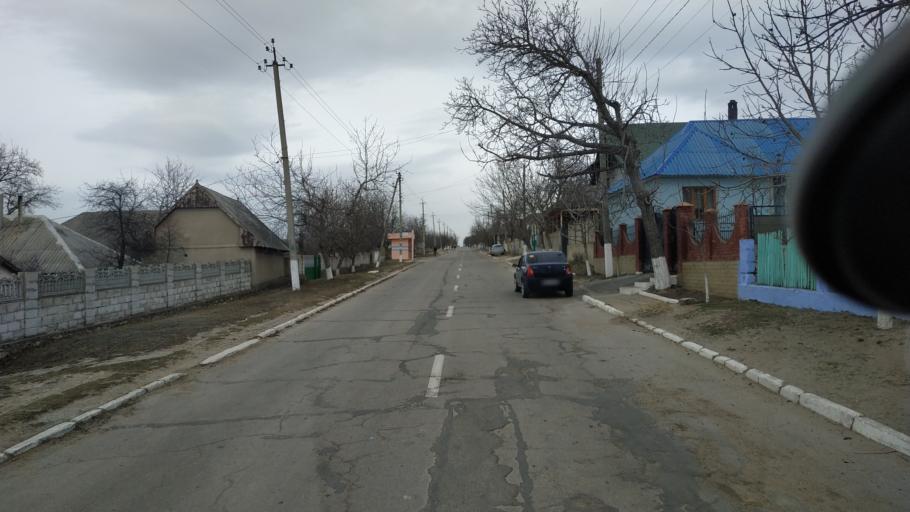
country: MD
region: Telenesti
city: Cocieri
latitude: 47.3475
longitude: 29.1176
